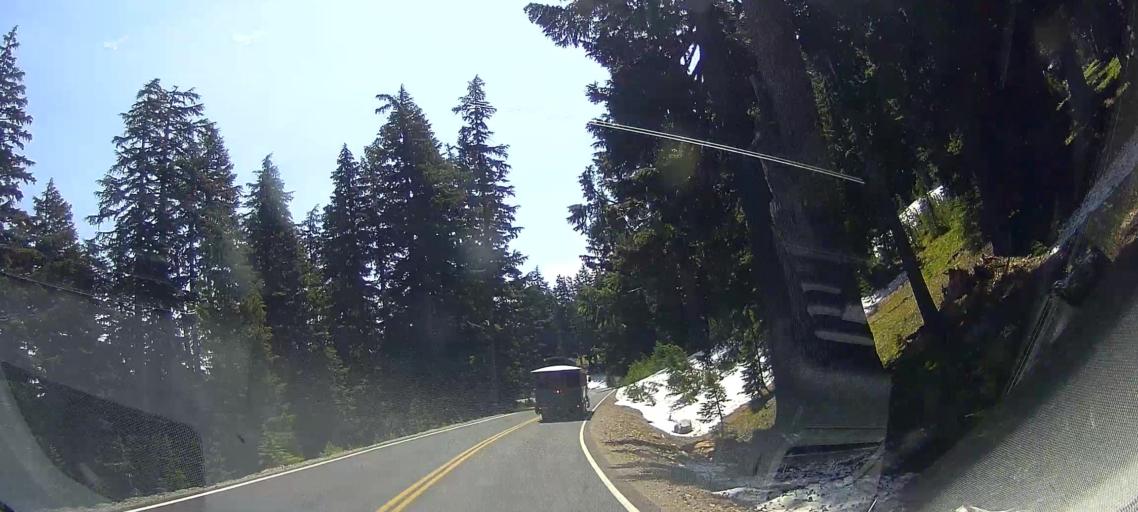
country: US
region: Oregon
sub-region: Jackson County
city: Shady Cove
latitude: 42.9809
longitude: -122.1224
